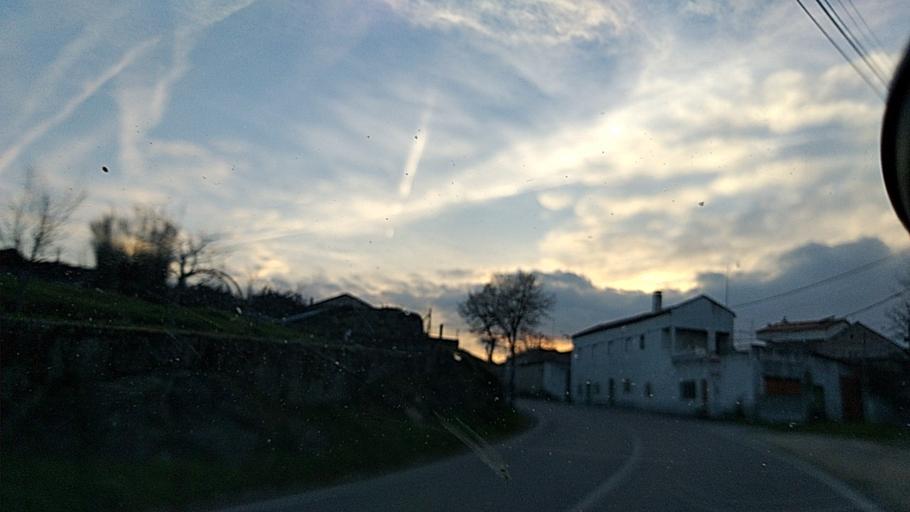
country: PT
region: Guarda
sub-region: Guarda
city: Sequeira
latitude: 40.5720
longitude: -7.2055
